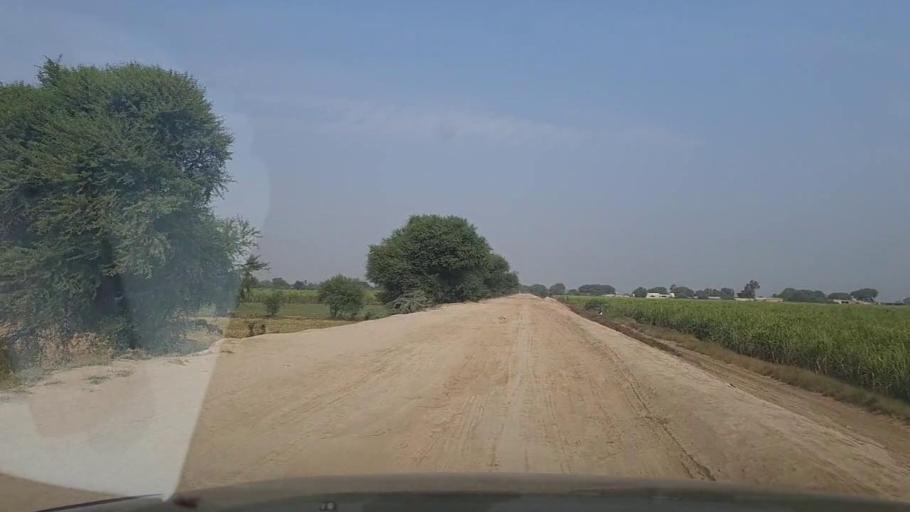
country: PK
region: Sindh
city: Bulri
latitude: 25.0200
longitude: 68.2834
